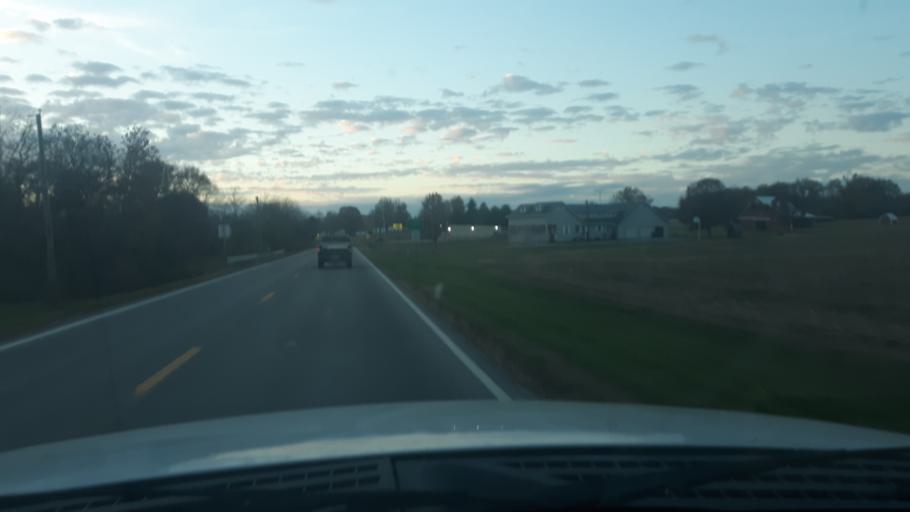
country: US
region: Illinois
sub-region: Saline County
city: Harrisburg
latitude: 37.8384
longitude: -88.5977
